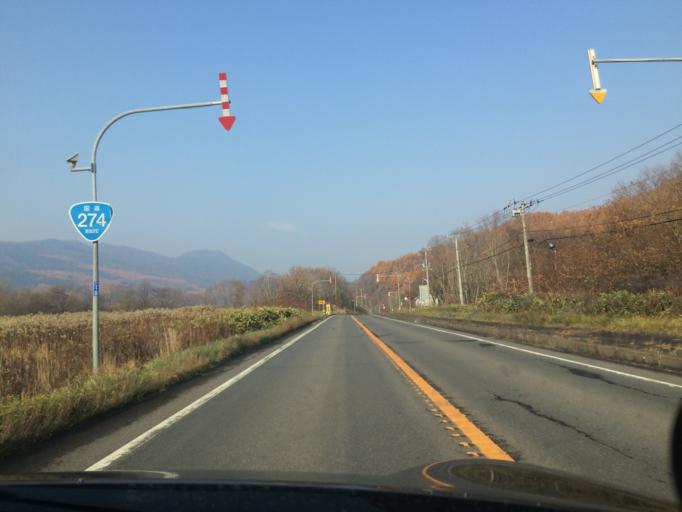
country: JP
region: Hokkaido
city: Iwamizawa
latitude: 42.9339
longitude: 142.0549
